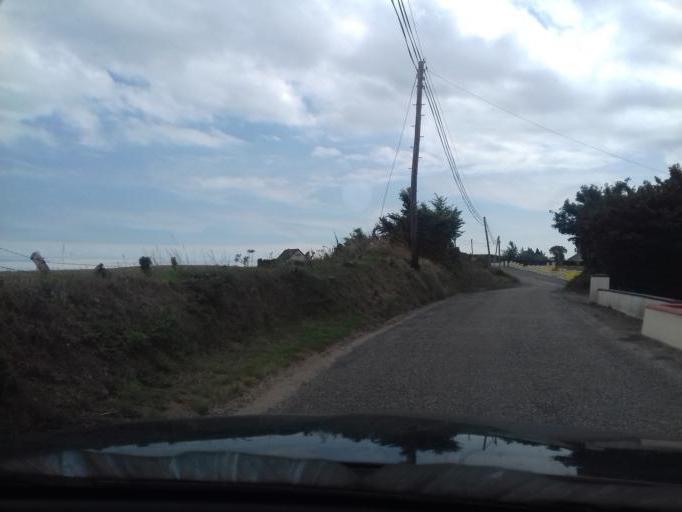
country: IE
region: Leinster
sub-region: Loch Garman
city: Castlebridge
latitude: 52.3997
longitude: -6.3967
